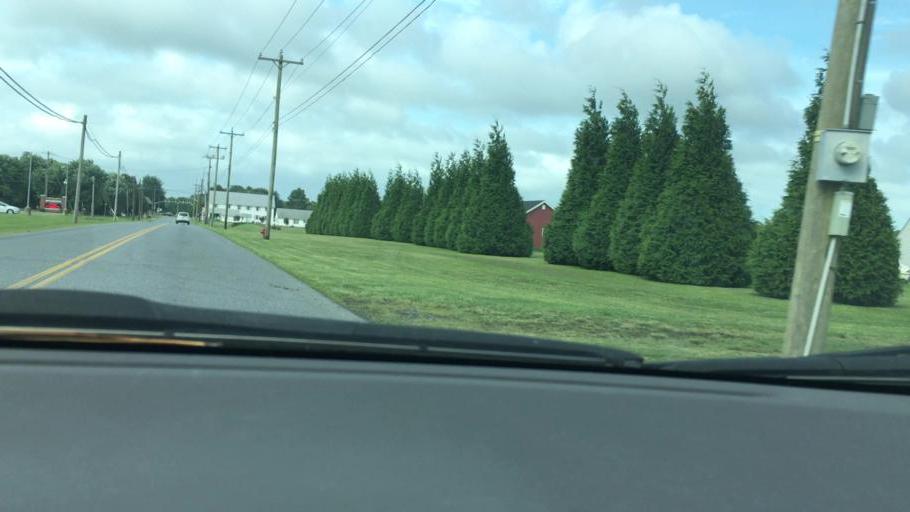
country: US
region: Maryland
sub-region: Worcester County
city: Pocomoke City
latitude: 38.0591
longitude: -75.5519
